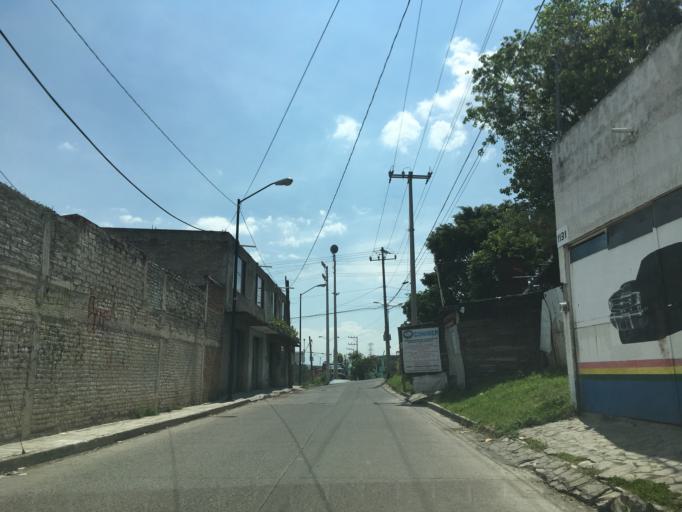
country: MX
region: Michoacan
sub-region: Morelia
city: Montana Monarca (Punta Altozano)
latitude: 19.6618
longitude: -101.1973
